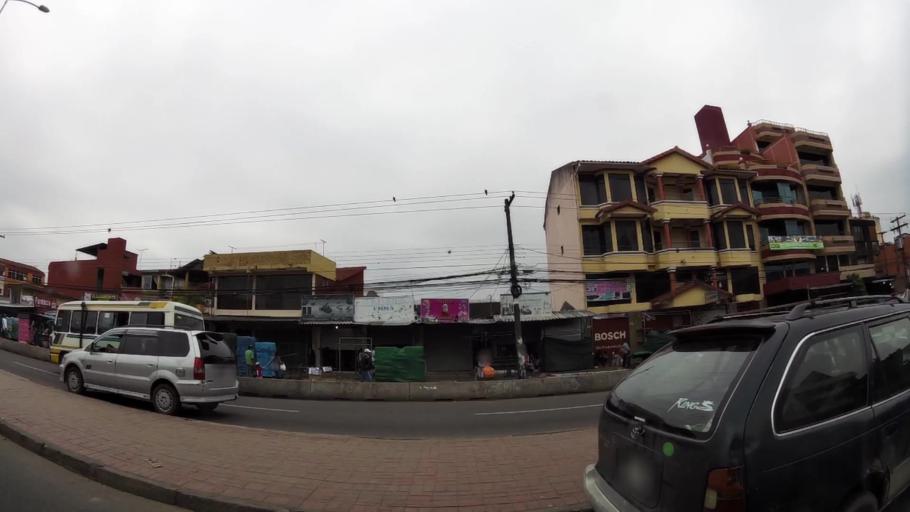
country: BO
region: Santa Cruz
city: Santa Cruz de la Sierra
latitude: -17.7951
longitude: -63.1890
